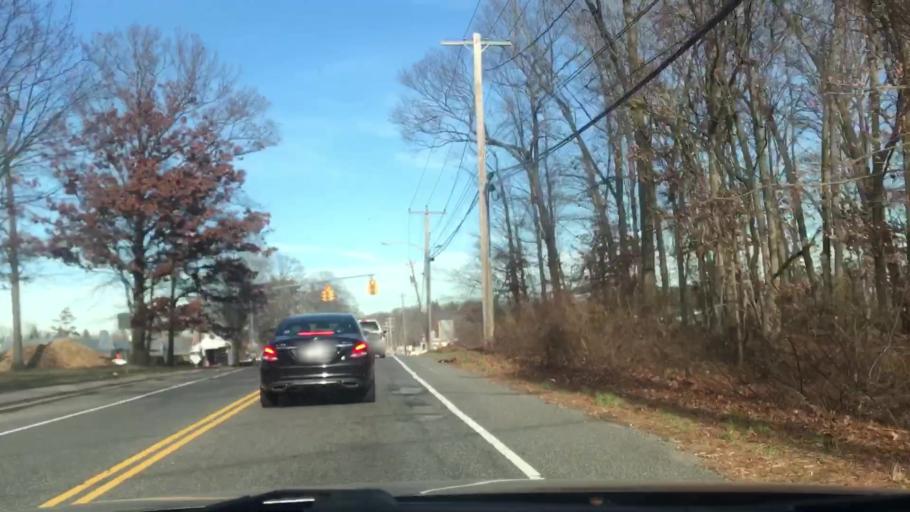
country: US
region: New York
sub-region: Suffolk County
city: Ronkonkoma
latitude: 40.8234
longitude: -73.1125
